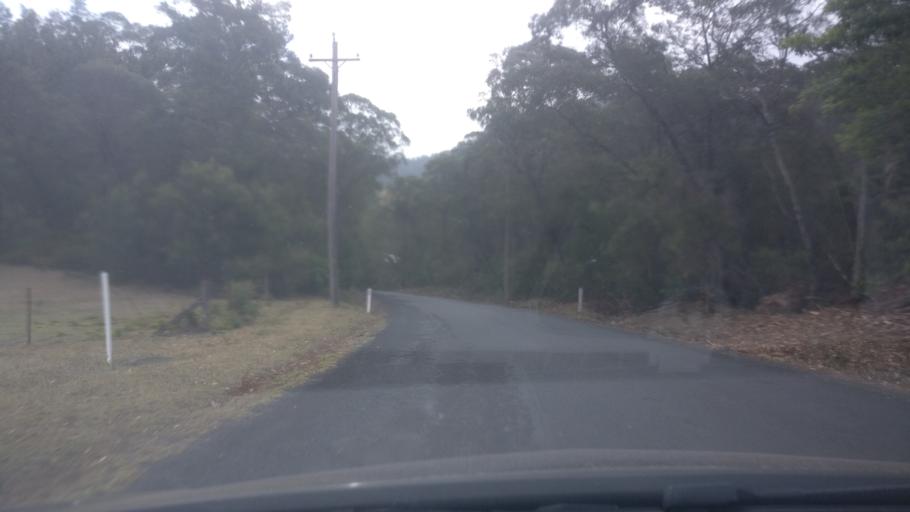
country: AU
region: New South Wales
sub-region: Shoalhaven Shire
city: Kangaroo Valley
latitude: -34.7227
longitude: 150.4778
